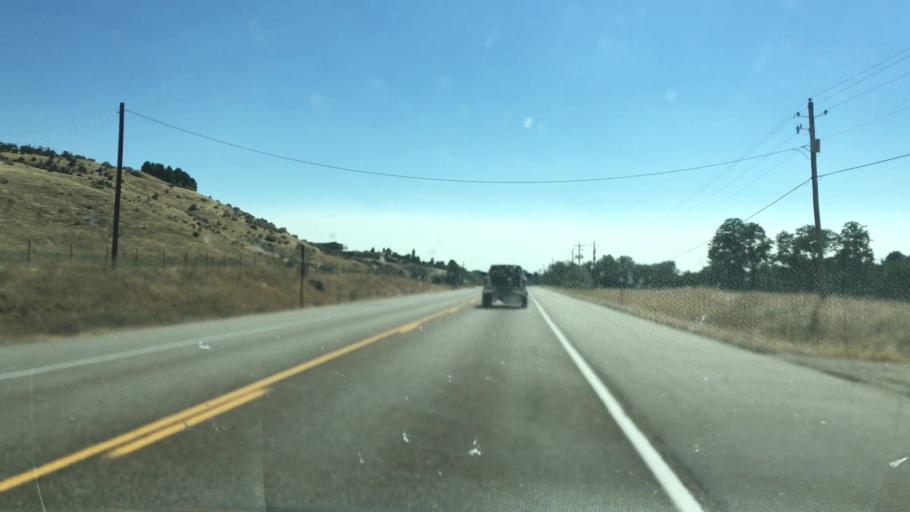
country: US
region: Idaho
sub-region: Ada County
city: Eagle
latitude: 43.7281
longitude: -116.3072
